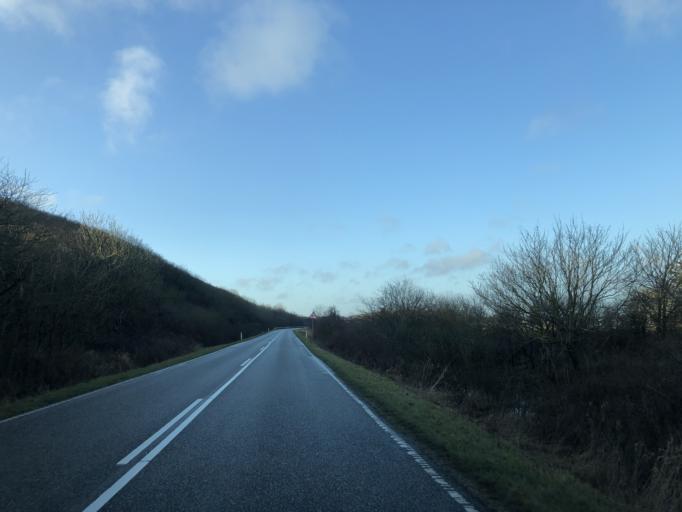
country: DK
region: Central Jutland
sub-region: Struer Kommune
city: Struer
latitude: 56.5410
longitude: 8.5108
